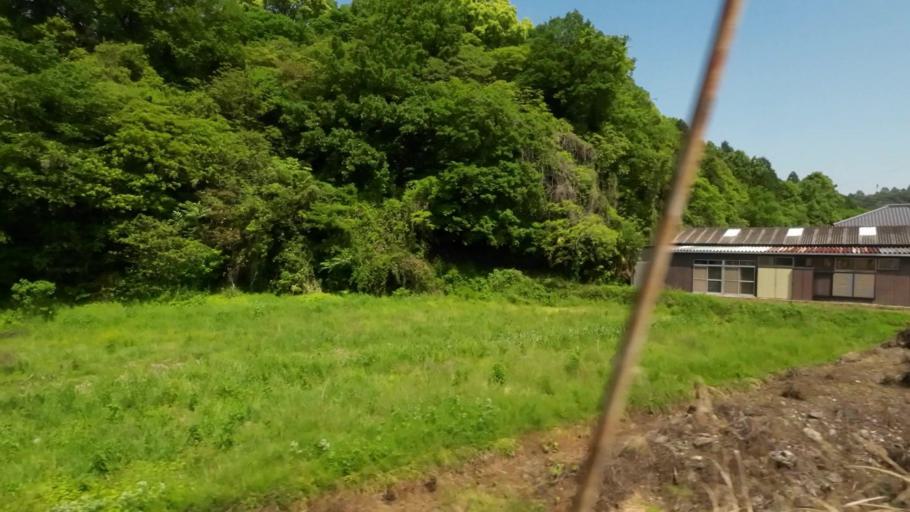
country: JP
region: Ehime
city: Saijo
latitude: 33.9228
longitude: 133.2462
